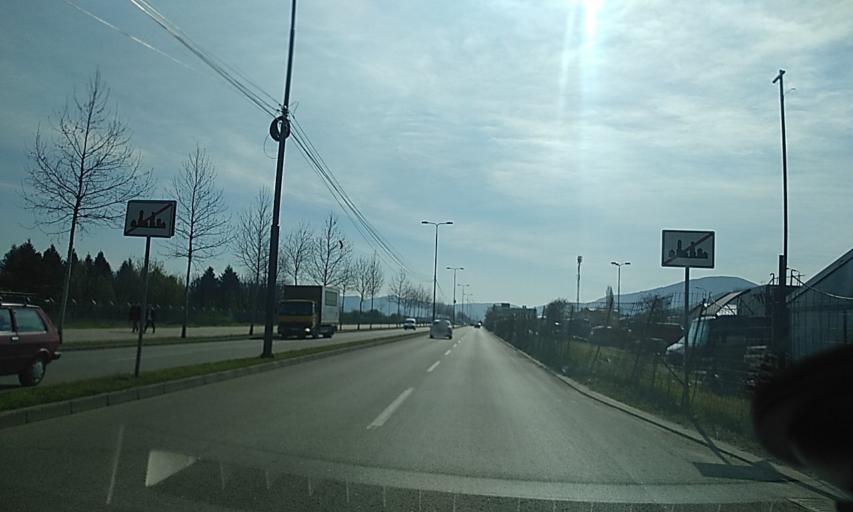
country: RS
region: Central Serbia
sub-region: Nisavski Okrug
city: Nis
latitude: 43.3097
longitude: 21.9386
